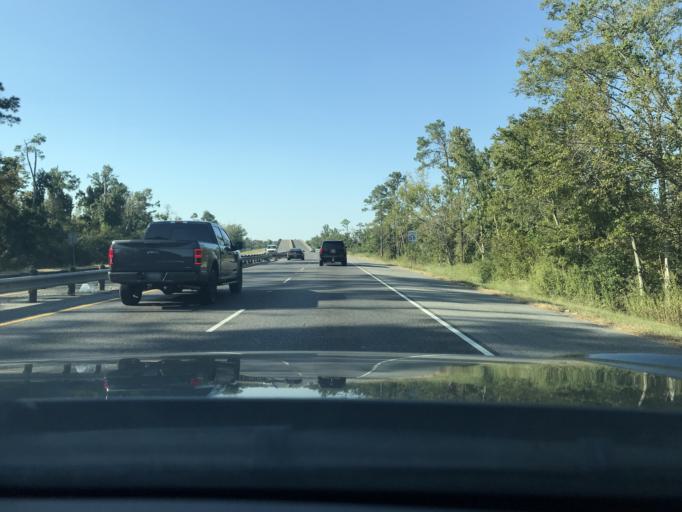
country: US
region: Louisiana
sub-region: Calcasieu Parish
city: Moss Bluff
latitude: 30.2805
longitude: -93.1849
